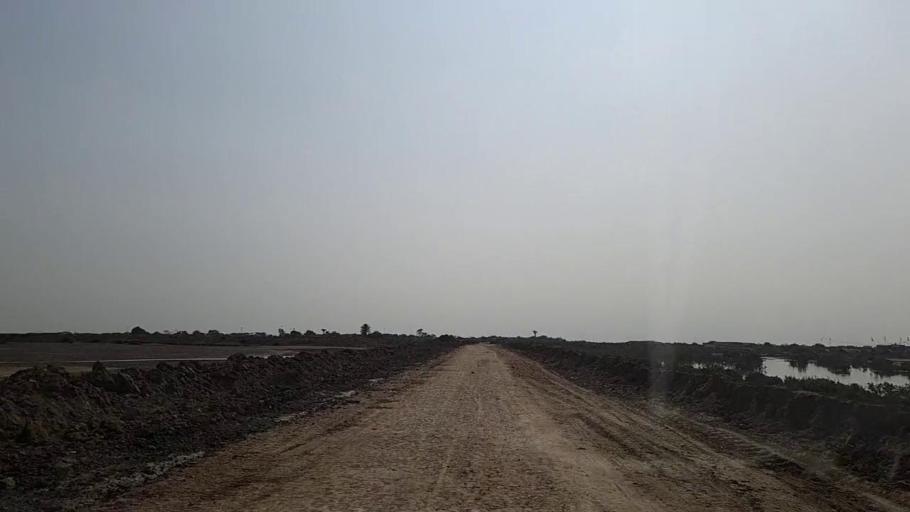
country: PK
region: Sindh
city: Chuhar Jamali
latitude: 24.1946
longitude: 67.8481
